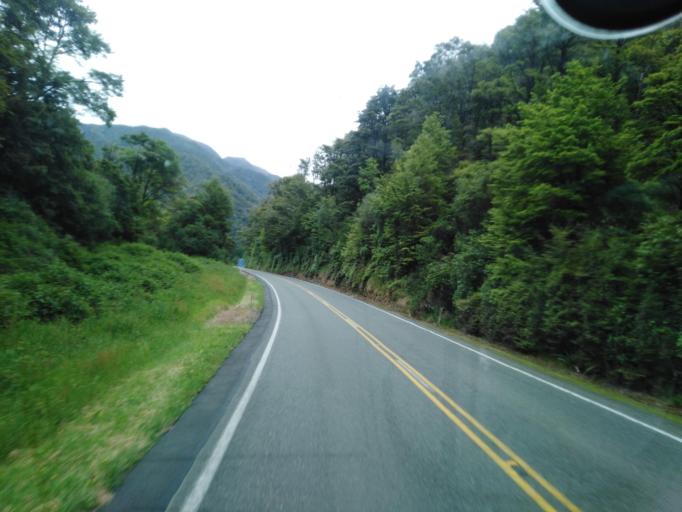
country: NZ
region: Tasman
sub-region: Tasman District
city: Wakefield
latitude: -41.7107
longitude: 172.5606
